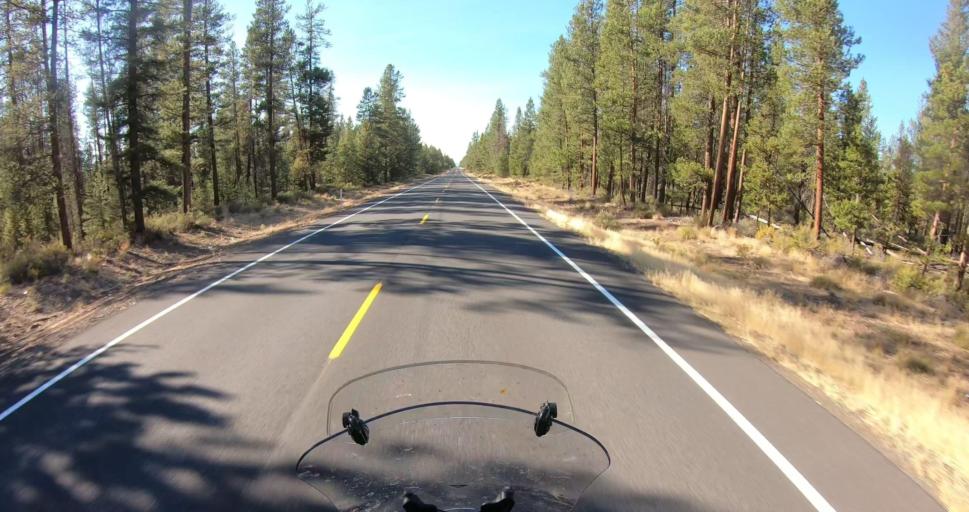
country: US
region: Oregon
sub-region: Deschutes County
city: La Pine
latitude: 43.4764
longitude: -121.4090
